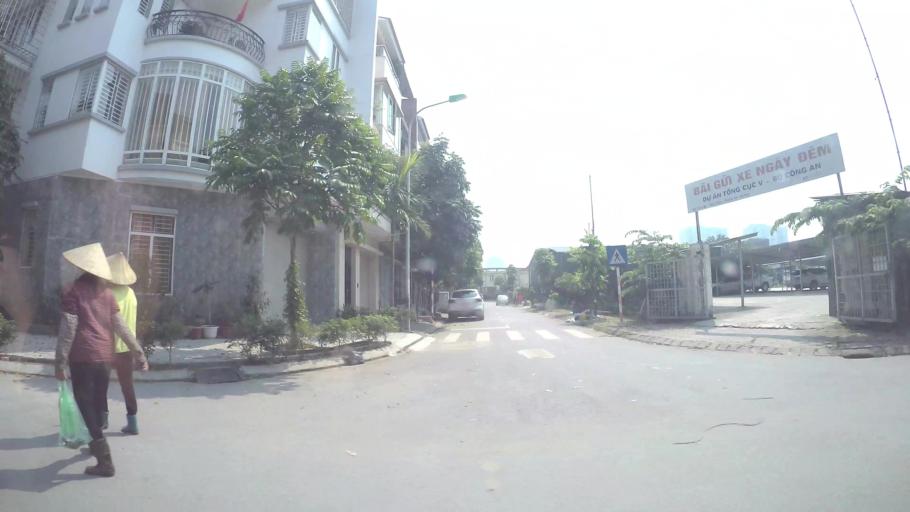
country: VN
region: Ha Noi
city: Ha Dong
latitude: 20.9689
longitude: 105.7989
